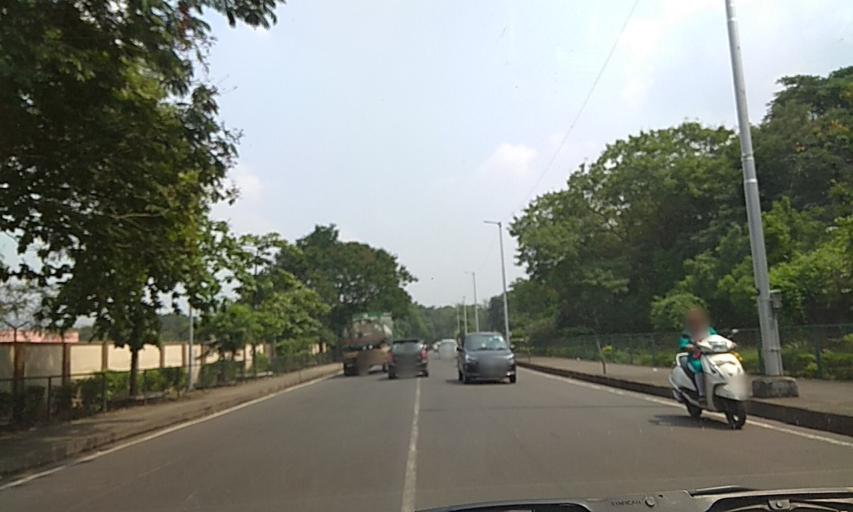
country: IN
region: Maharashtra
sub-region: Pune Division
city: Shivaji Nagar
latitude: 18.5380
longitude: 73.8005
